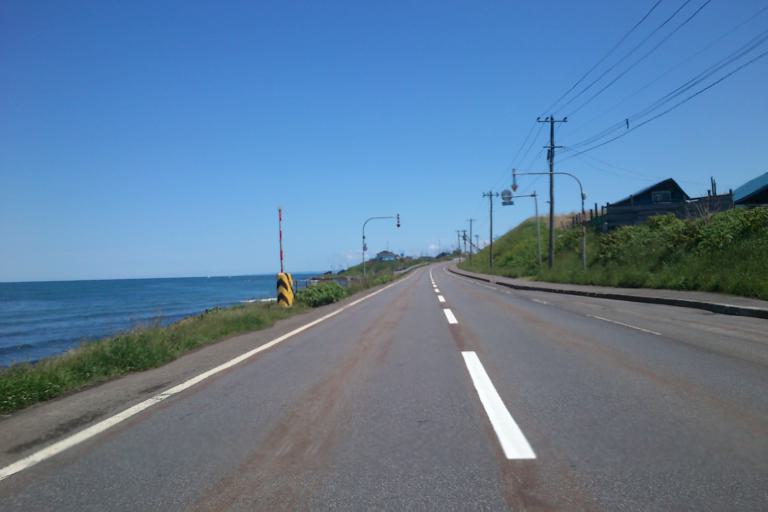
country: JP
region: Hokkaido
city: Rumoi
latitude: 43.8434
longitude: 141.5005
